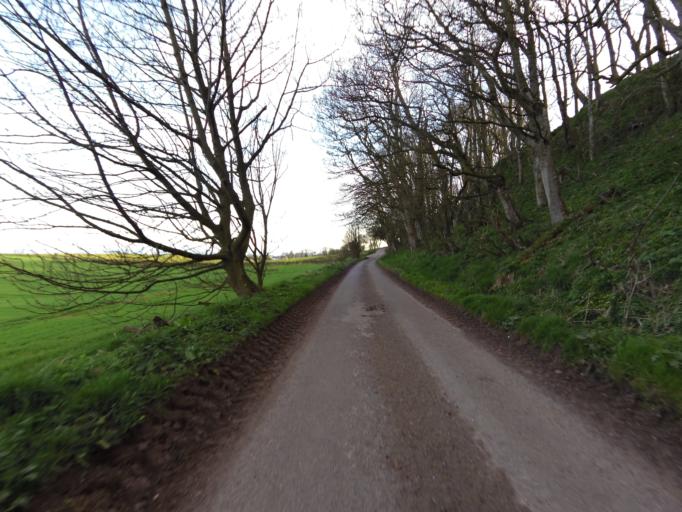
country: GB
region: Scotland
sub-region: Aberdeenshire
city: Inverbervie
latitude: 56.8703
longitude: -2.2368
